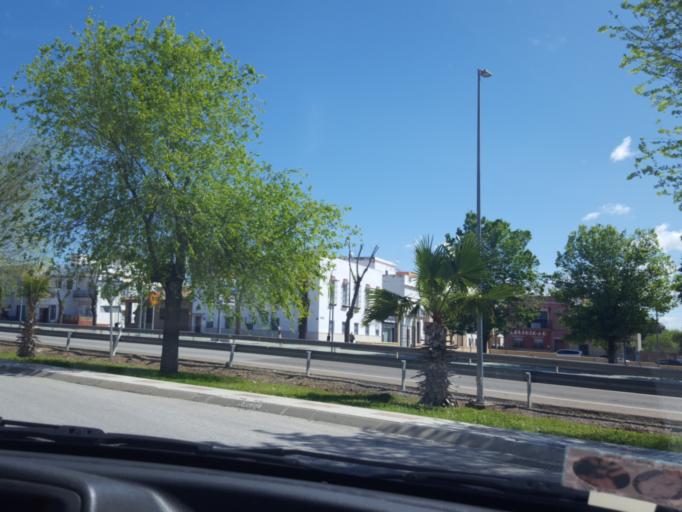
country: ES
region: Andalusia
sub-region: Provincia de Sevilla
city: Acala del Rio
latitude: 37.5148
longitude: -5.9865
